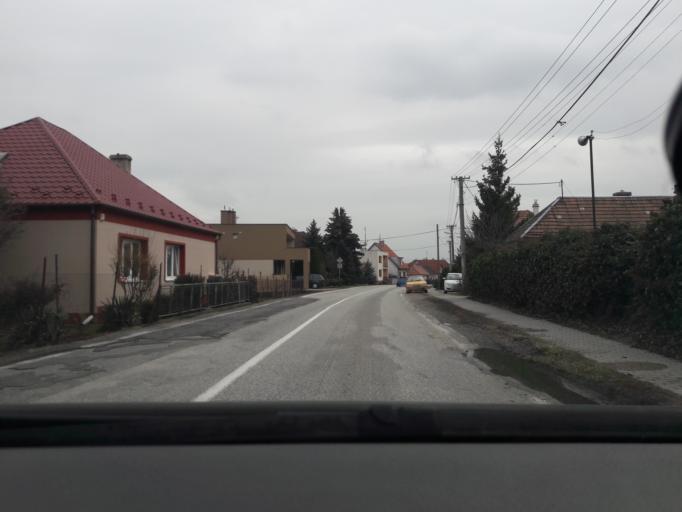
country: SK
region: Trnavsky
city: Smolenice
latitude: 48.4141
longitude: 17.3810
